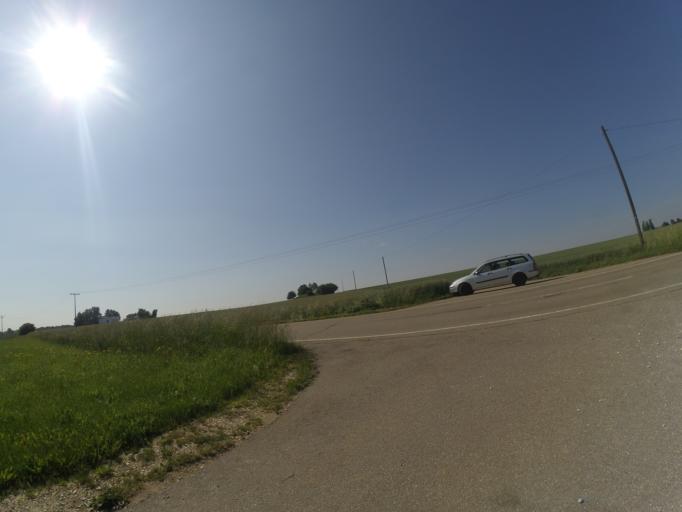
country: DE
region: Baden-Wuerttemberg
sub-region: Tuebingen Region
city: Beimerstetten
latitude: 48.4827
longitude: 9.9944
